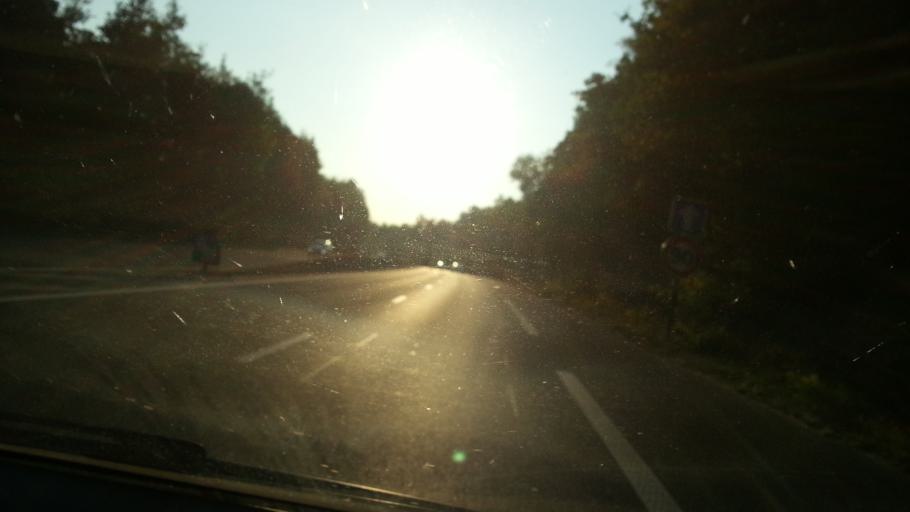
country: FR
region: Picardie
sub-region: Departement de l'Oise
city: Cinqueux
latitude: 49.3061
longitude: 2.5308
